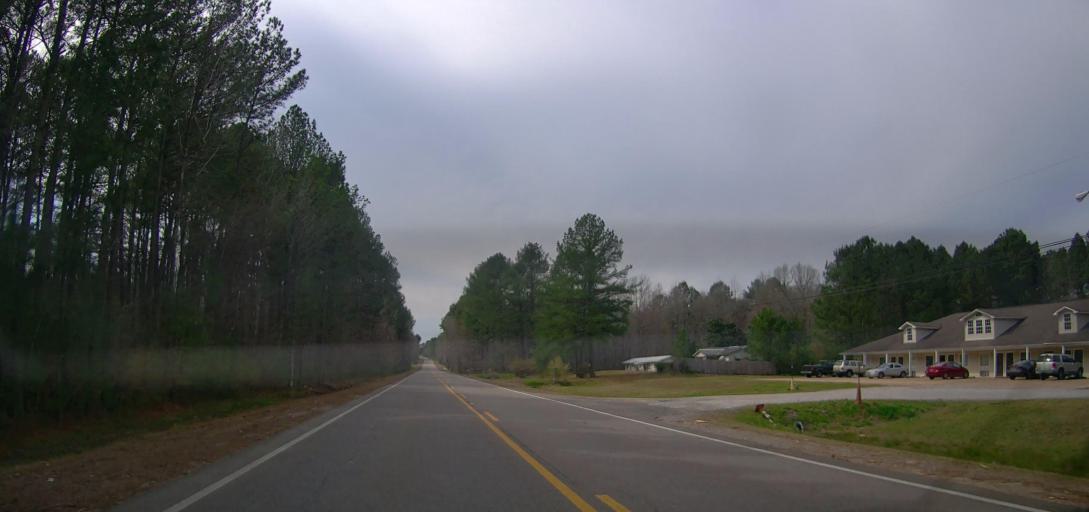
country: US
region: Alabama
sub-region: Walker County
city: Carbon Hill
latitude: 33.8750
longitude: -87.4634
